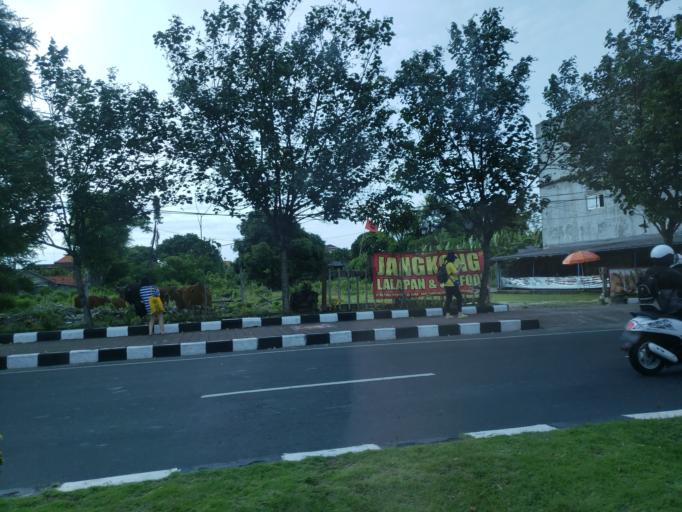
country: ID
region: Bali
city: Jabajero
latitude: -8.7258
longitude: 115.1807
